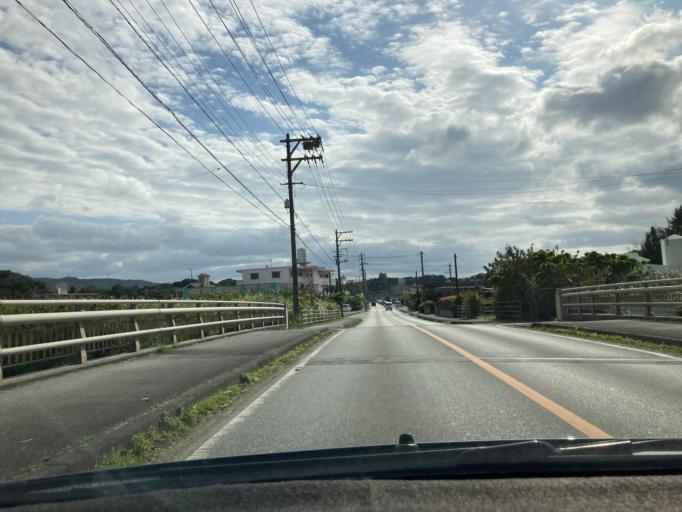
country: JP
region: Okinawa
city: Nago
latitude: 26.6254
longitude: 128.0020
